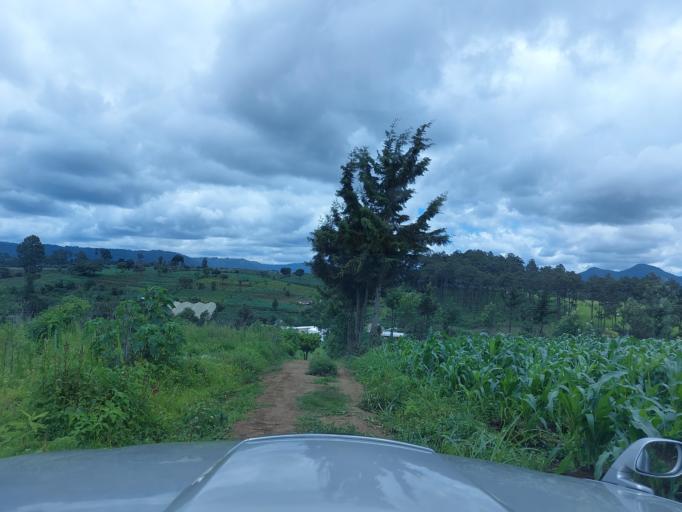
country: GT
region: Chimaltenango
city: San Andres Itzapa
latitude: 14.6394
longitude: -90.8307
